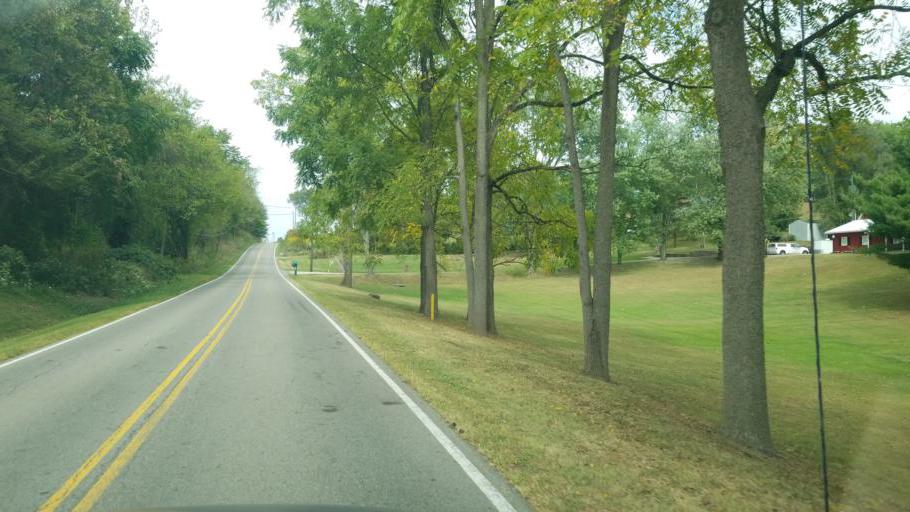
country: US
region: Ohio
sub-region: Licking County
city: Newark
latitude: 40.0857
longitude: -82.3871
